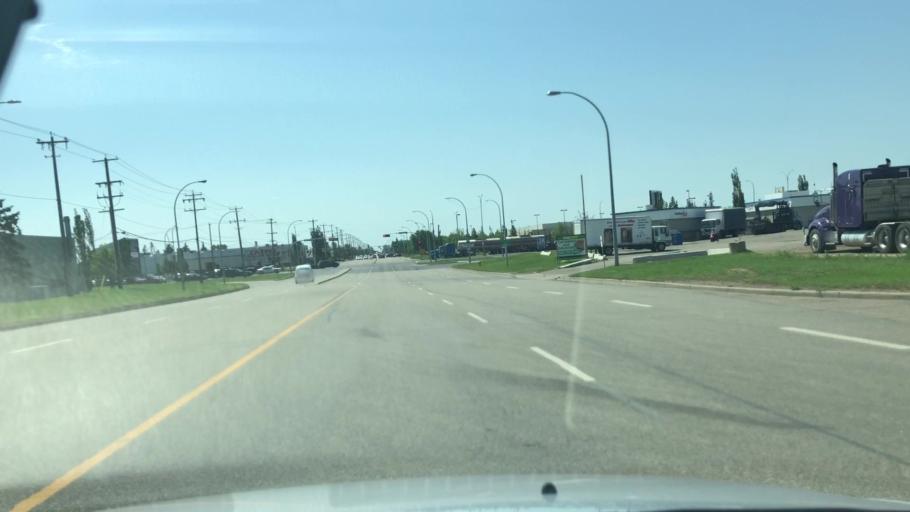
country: CA
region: Alberta
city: St. Albert
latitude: 53.5836
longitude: -113.5782
